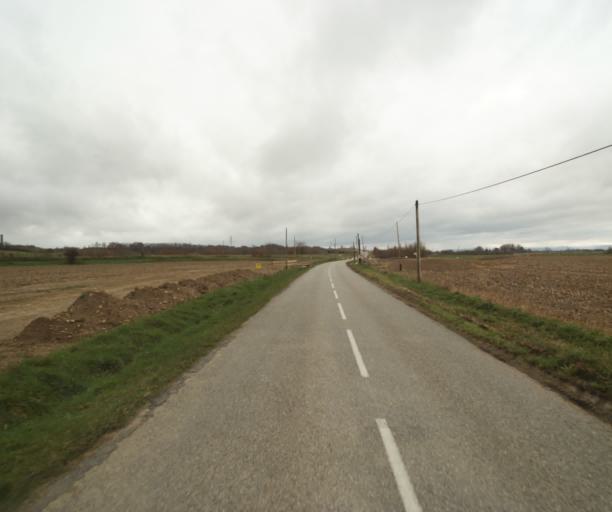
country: FR
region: Midi-Pyrenees
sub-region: Departement de l'Ariege
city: Saverdun
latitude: 43.2016
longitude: 1.6283
